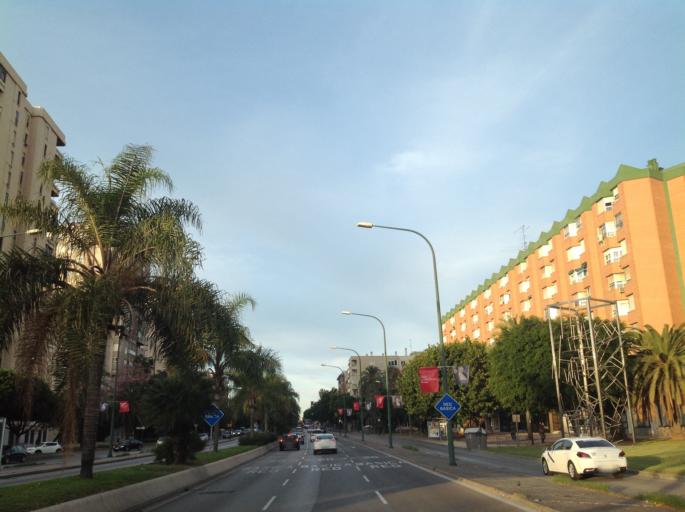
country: ES
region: Andalusia
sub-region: Provincia de Malaga
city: Malaga
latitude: 36.7171
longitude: -4.4372
